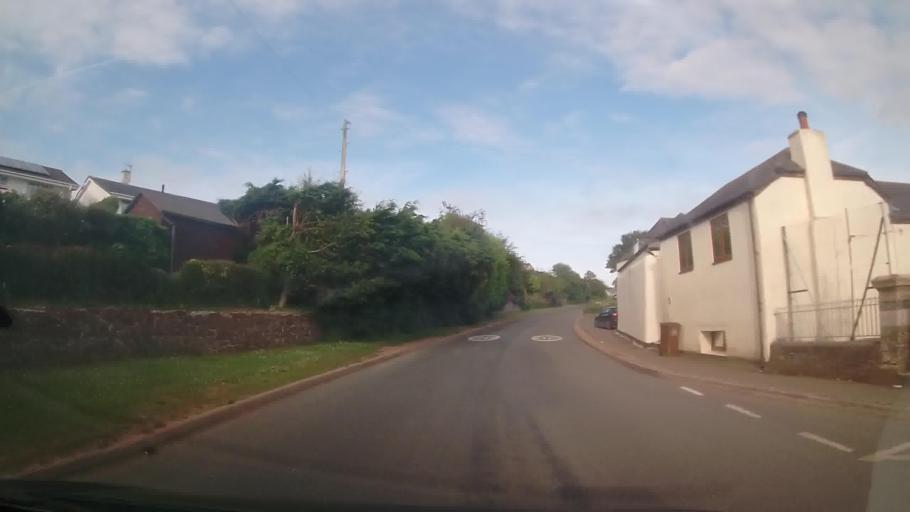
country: GB
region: England
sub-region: Devon
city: Kingsbridge
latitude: 50.2707
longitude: -3.7484
